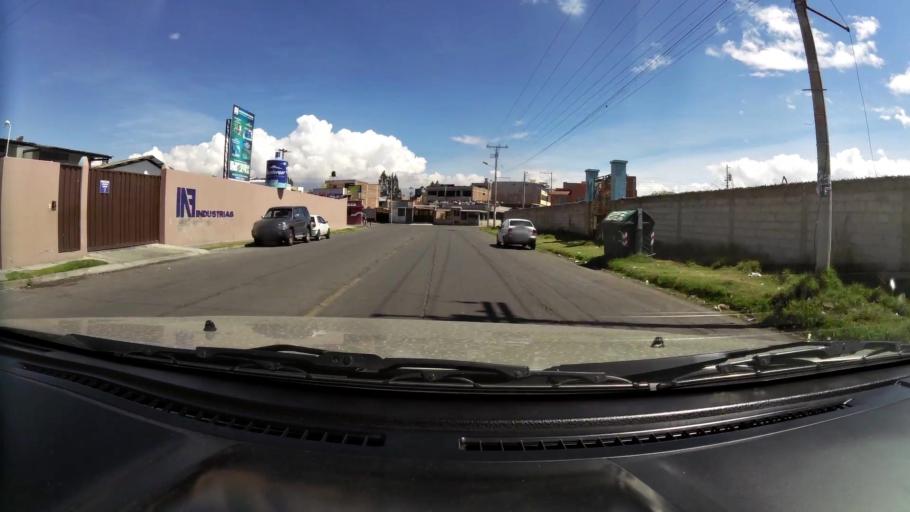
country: EC
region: Chimborazo
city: Riobamba
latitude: -1.6770
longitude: -78.6319
